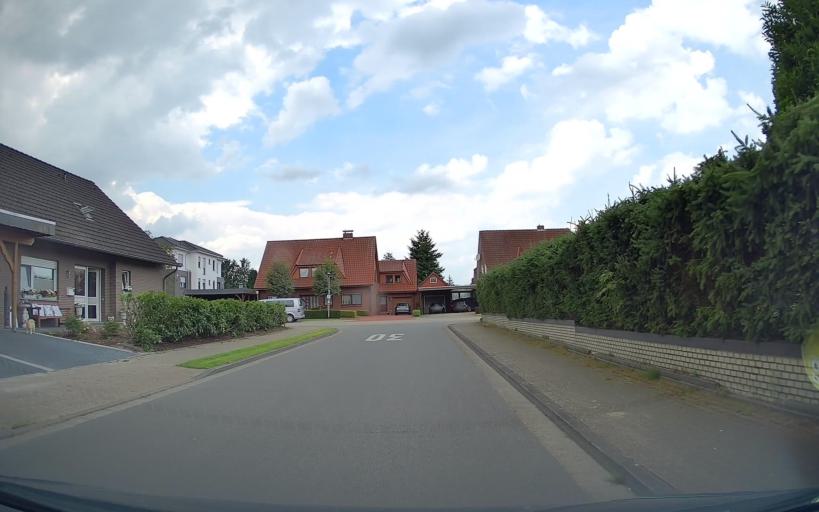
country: DE
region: Lower Saxony
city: Bosel
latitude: 53.0019
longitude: 7.9565
